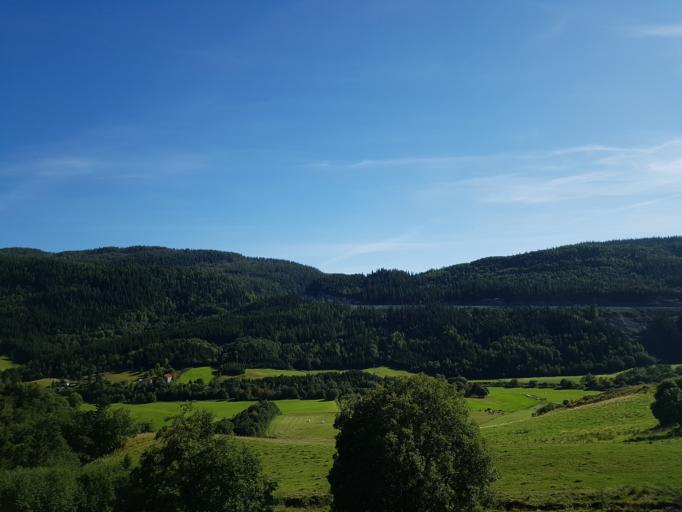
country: NO
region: Sor-Trondelag
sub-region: Afjord
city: A i Afjord
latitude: 63.6804
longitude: 10.2307
